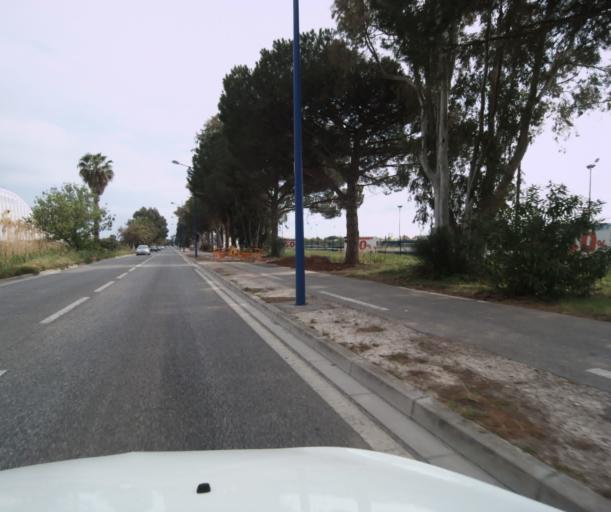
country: FR
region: Provence-Alpes-Cote d'Azur
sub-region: Departement du Var
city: Hyeres
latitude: 43.0903
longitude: 6.1434
